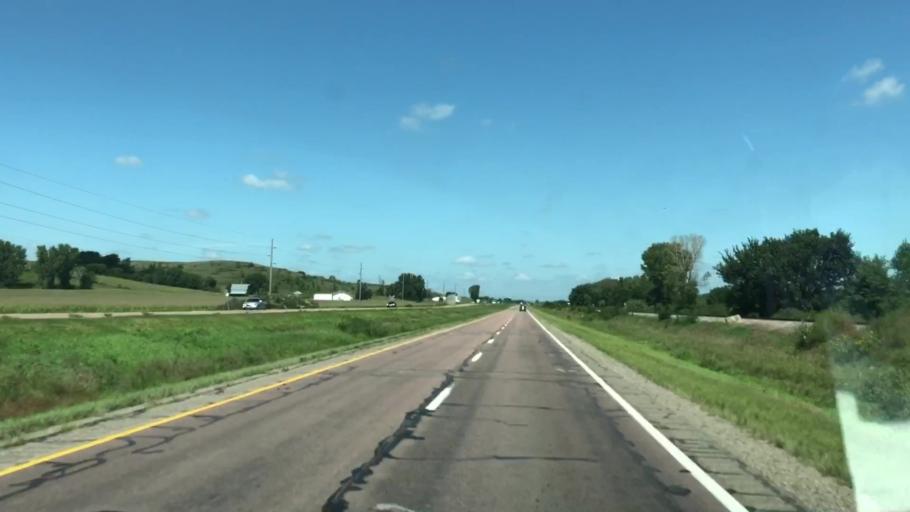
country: US
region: Iowa
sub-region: Woodbury County
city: Sioux City
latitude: 42.6363
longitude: -96.2893
